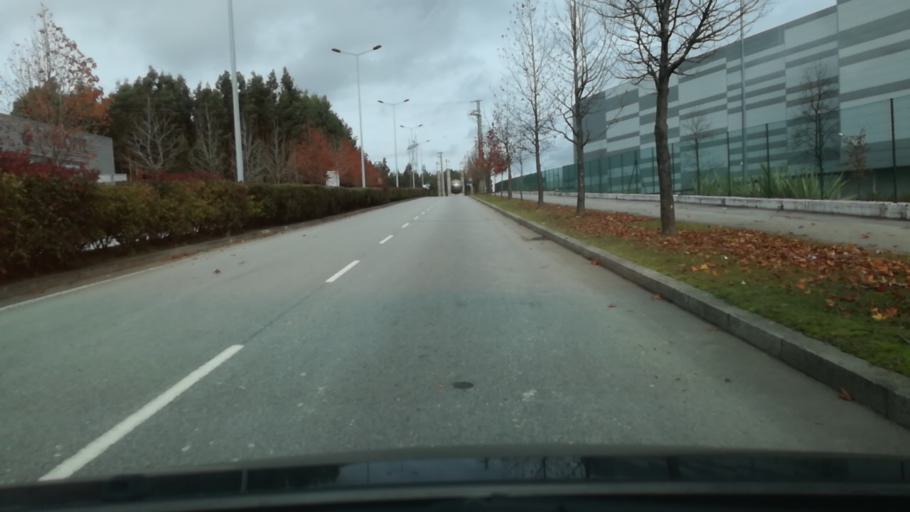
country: PT
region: Porto
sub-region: Maia
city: Maia
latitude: 41.2429
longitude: -8.6304
